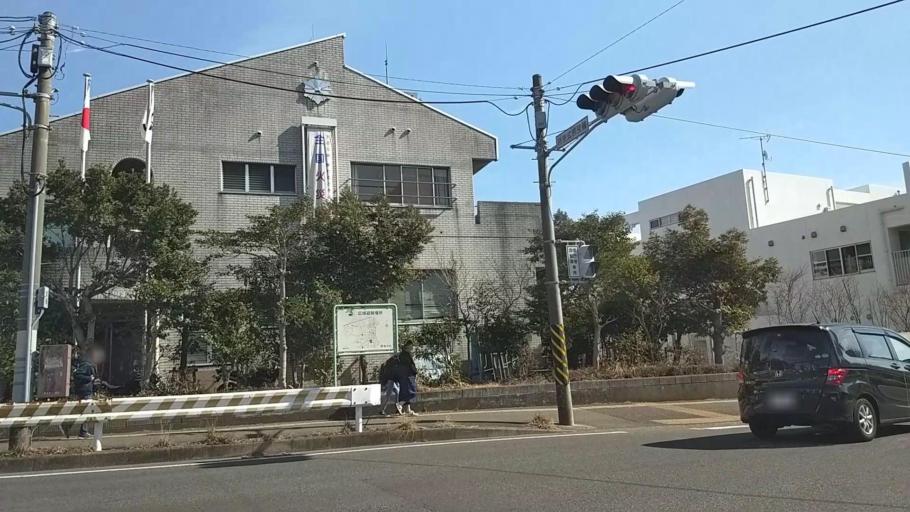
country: JP
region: Kanagawa
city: Fujisawa
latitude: 35.3637
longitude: 139.4455
